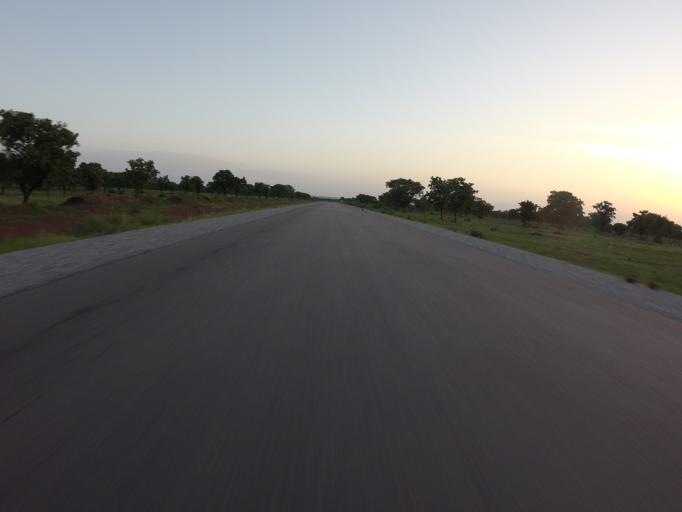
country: GH
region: Northern
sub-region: Yendi
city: Yendi
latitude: 9.9443
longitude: -0.1632
